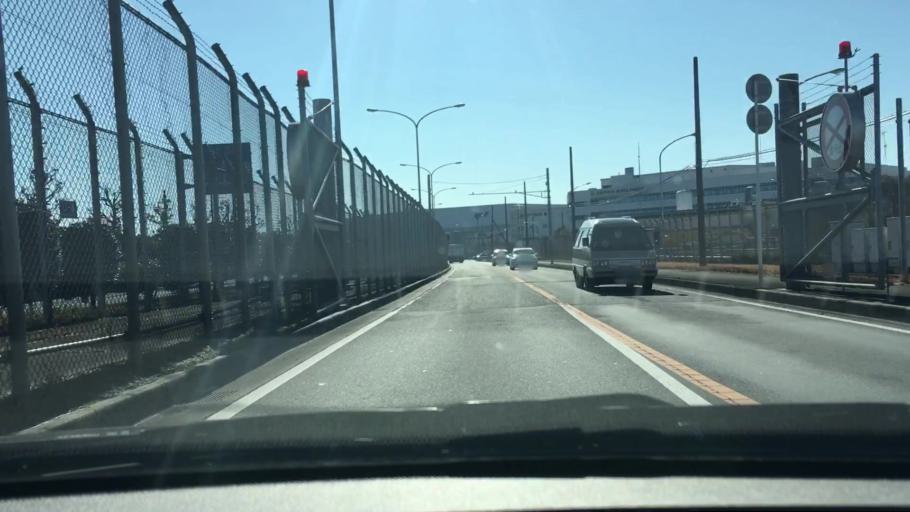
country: JP
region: Chiba
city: Narita
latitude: 35.7519
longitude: 140.4007
